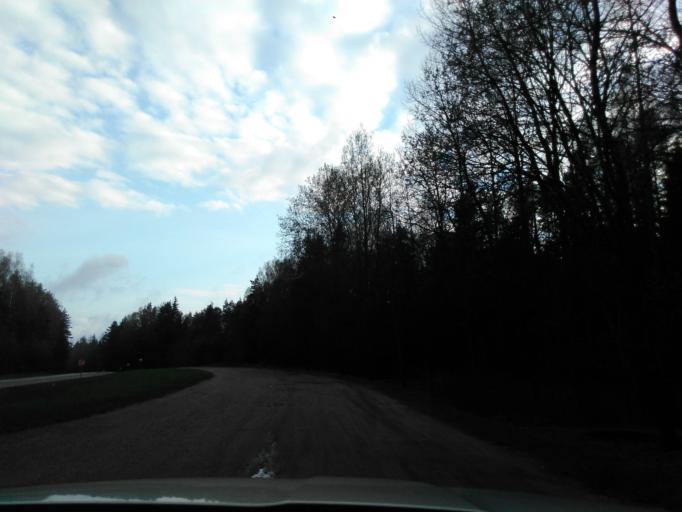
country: BY
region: Minsk
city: Lahoysk
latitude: 54.2811
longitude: 27.8634
